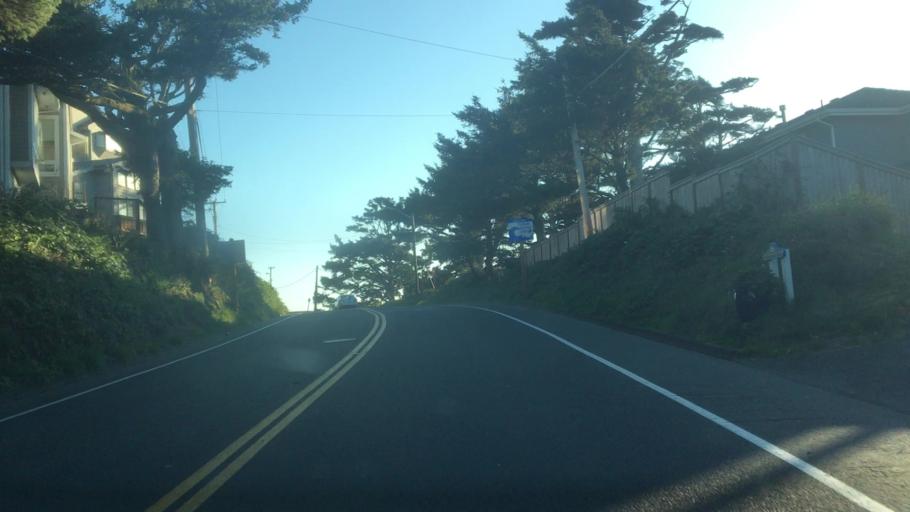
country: US
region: Oregon
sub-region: Clatsop County
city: Cannon Beach
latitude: 45.8856
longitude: -123.9631
